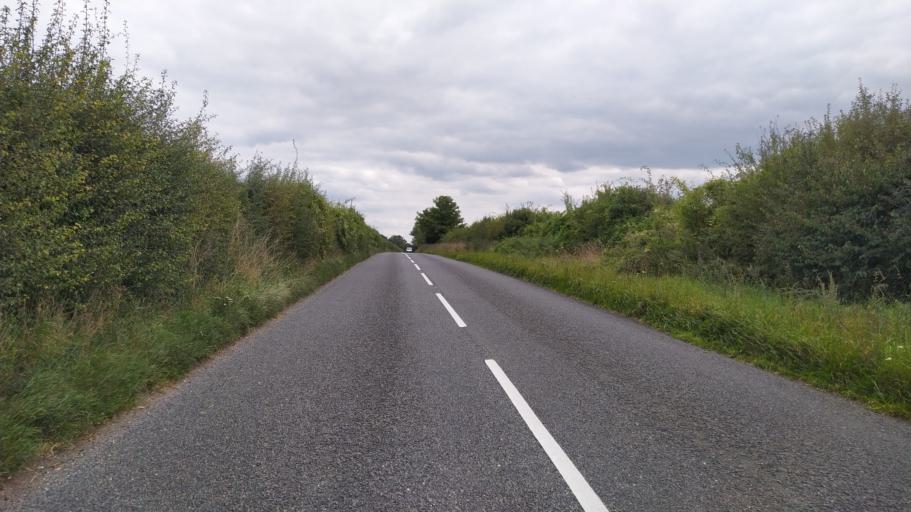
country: GB
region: England
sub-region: Wiltshire
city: Tidworth
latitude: 51.1757
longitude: -1.6389
